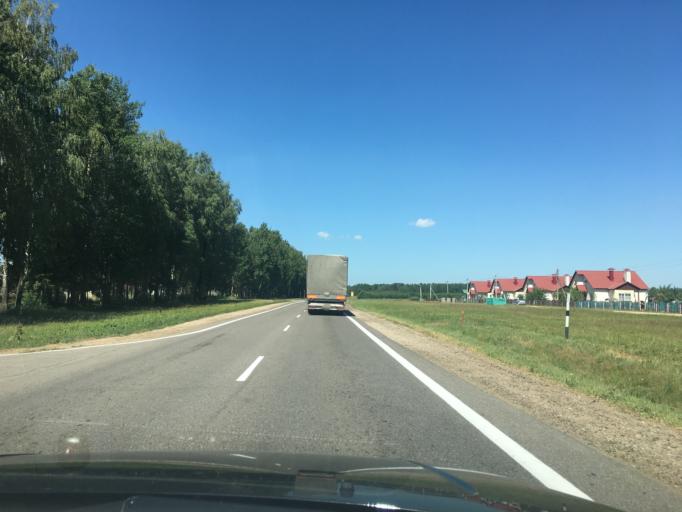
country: BY
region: Grodnenskaya
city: Iwye
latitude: 54.0369
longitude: 25.9206
